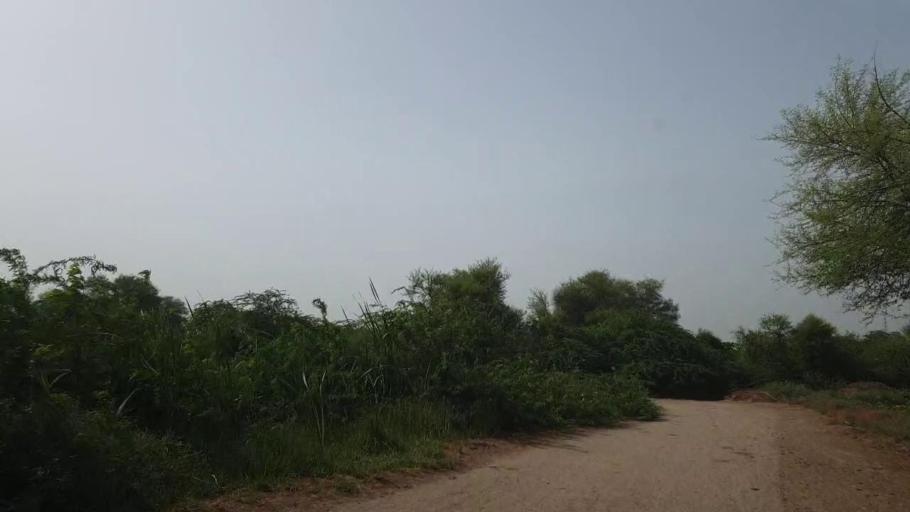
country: PK
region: Sindh
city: Nawabshah
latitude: 26.1153
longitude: 68.4336
